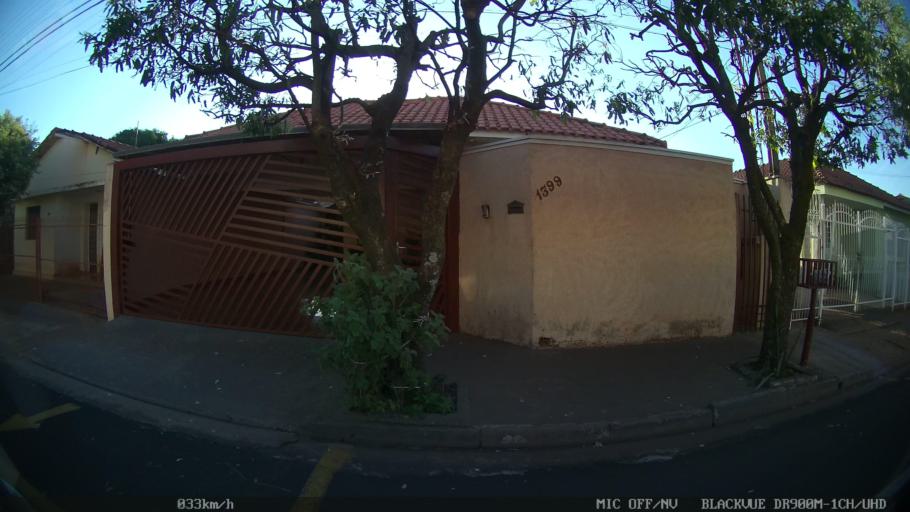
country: BR
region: Sao Paulo
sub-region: Sao Jose Do Rio Preto
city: Sao Jose do Rio Preto
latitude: -20.7918
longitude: -49.3640
